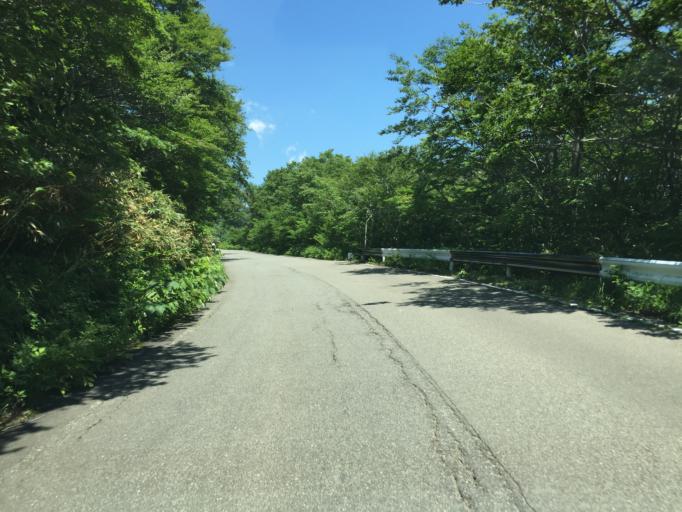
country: JP
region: Fukushima
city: Nihommatsu
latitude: 37.6619
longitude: 140.2855
